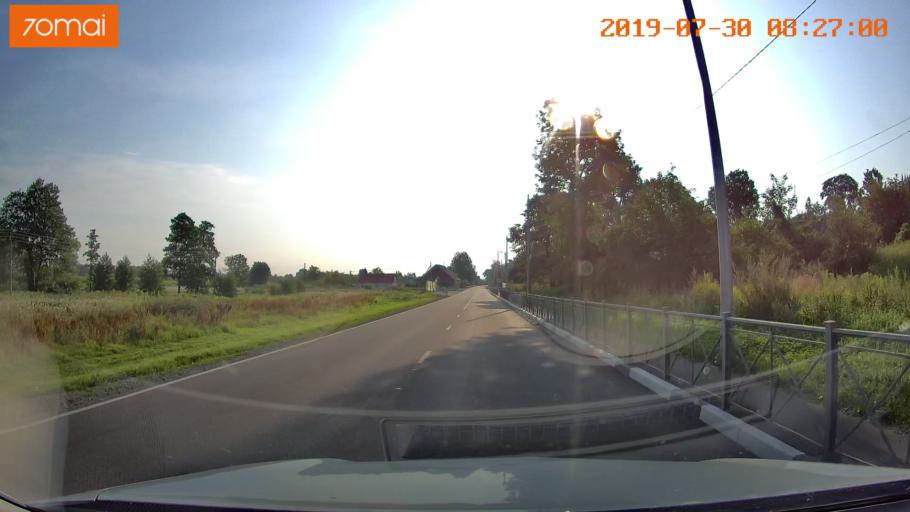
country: RU
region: Kaliningrad
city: Chernyakhovsk
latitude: 54.6265
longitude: 21.6163
